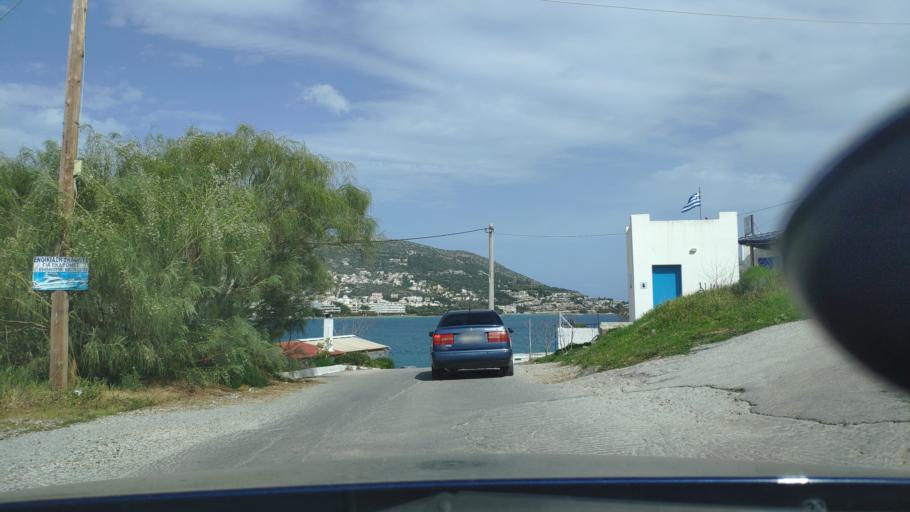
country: GR
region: Attica
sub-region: Nomarchia Anatolikis Attikis
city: Limin Mesoyaias
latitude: 37.8863
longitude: 24.0150
